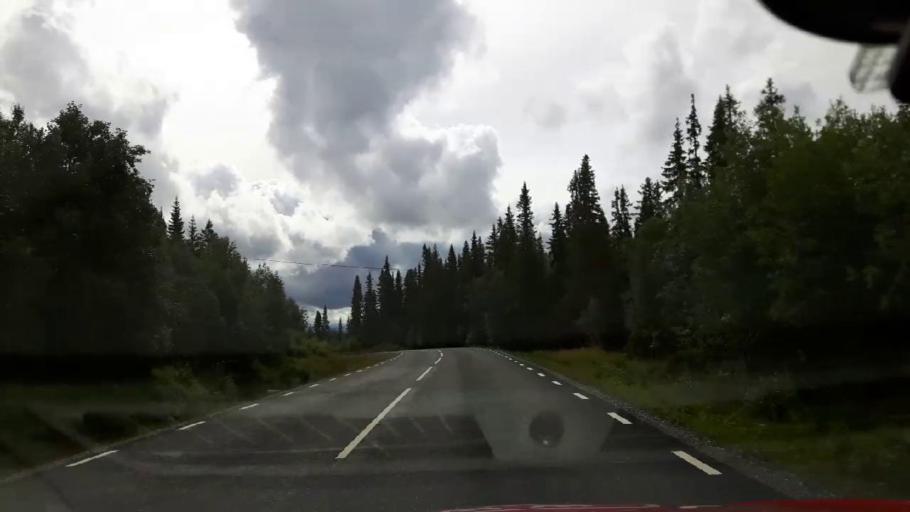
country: NO
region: Nord-Trondelag
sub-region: Lierne
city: Sandvika
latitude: 64.6109
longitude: 14.1189
